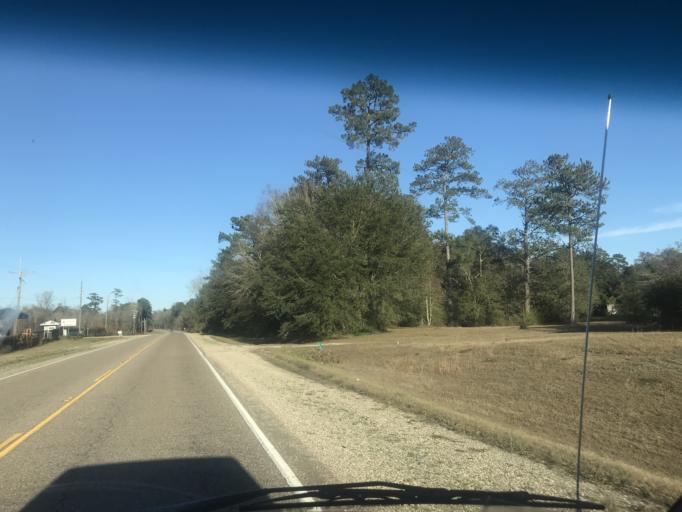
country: US
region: Louisiana
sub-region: Washington Parish
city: Franklinton
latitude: 30.6815
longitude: -90.1905
